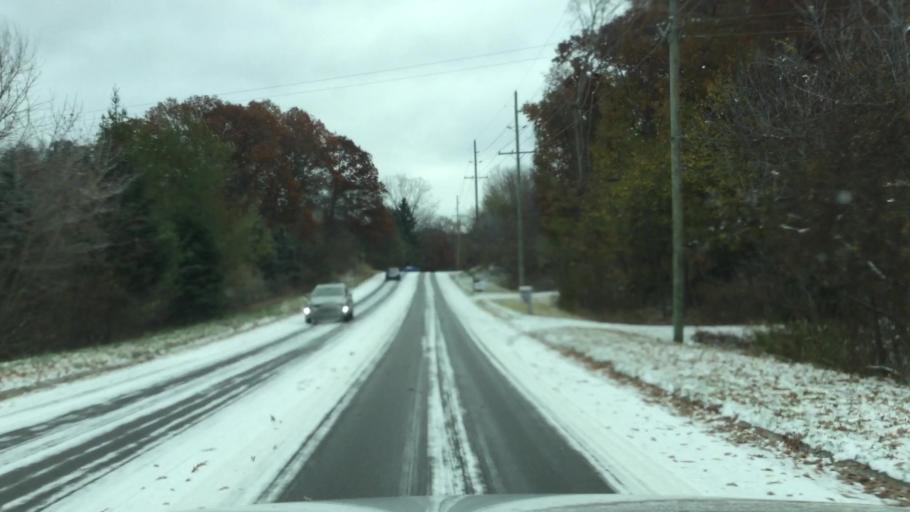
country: US
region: Michigan
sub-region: Livingston County
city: Brighton
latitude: 42.5282
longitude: -83.8307
